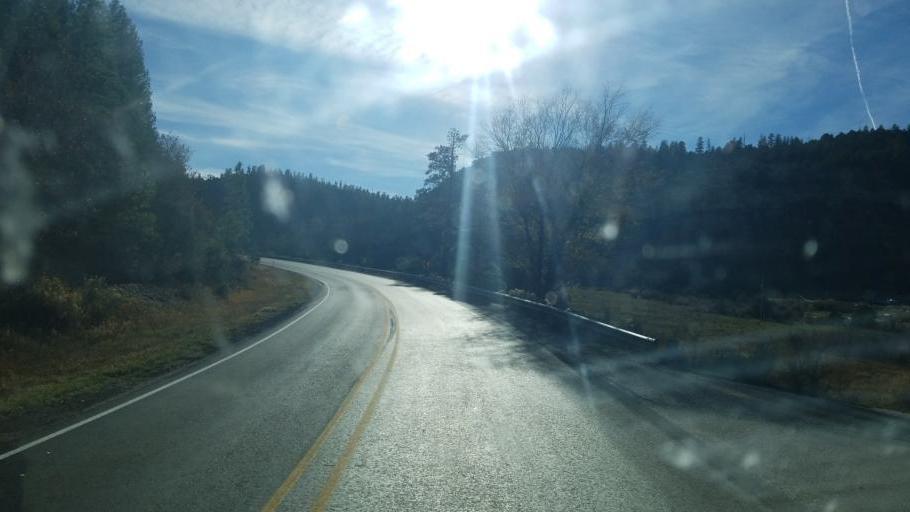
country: US
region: New Mexico
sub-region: Rio Arriba County
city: Dulce
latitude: 36.9106
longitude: -107.0000
